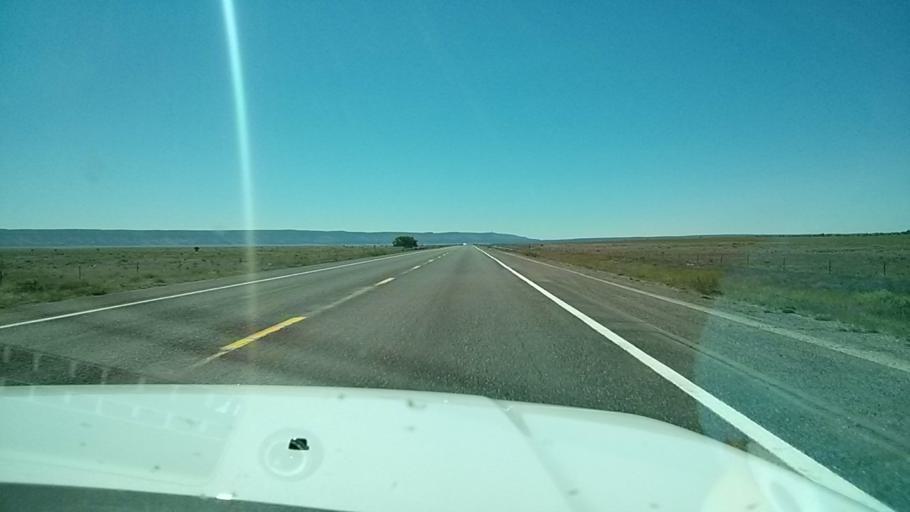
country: US
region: Arizona
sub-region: Mohave County
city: Peach Springs
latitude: 35.4564
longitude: -113.1032
